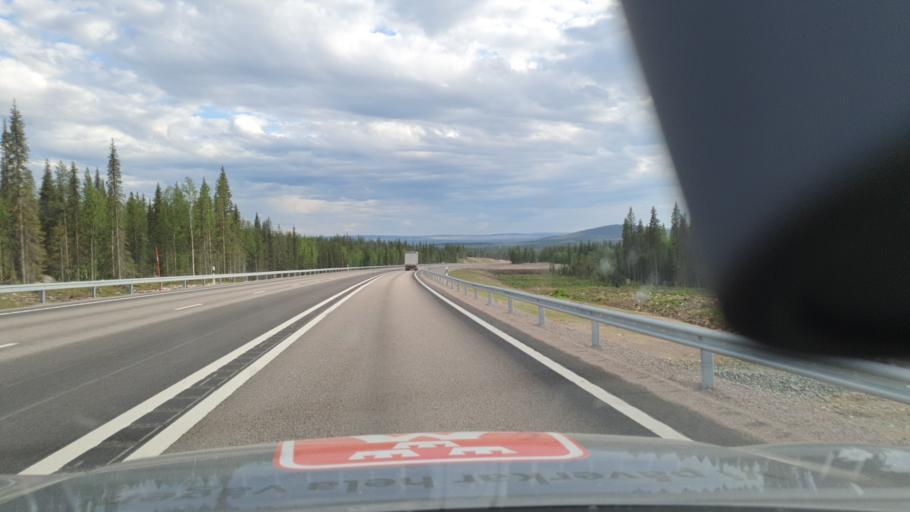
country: SE
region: Norrbotten
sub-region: Gallivare Kommun
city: Malmberget
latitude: 67.1863
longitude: 20.9764
